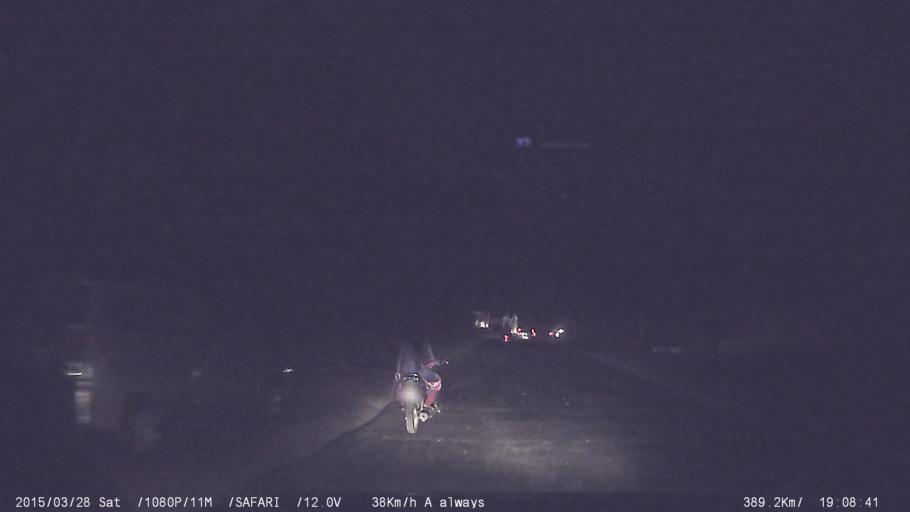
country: IN
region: Karnataka
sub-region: Mandya
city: Shrirangapattana
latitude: 12.3923
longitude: 76.6217
